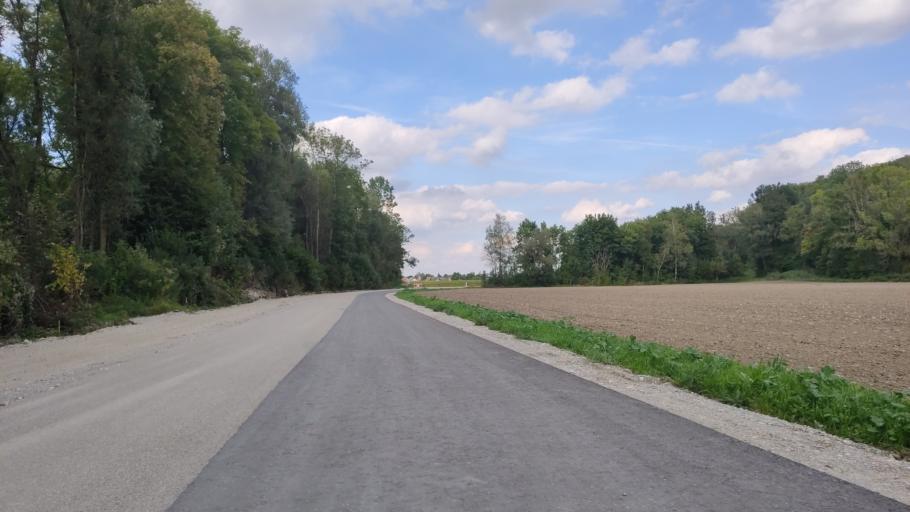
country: DE
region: Bavaria
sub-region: Upper Bavaria
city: Scheuring
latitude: 48.1596
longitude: 10.8802
